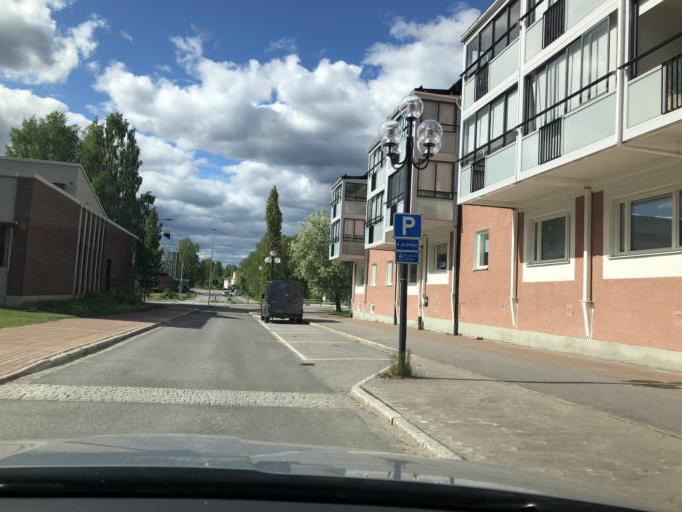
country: SE
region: Norrbotten
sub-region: Alvsbyns Kommun
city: AElvsbyn
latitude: 65.6743
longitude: 21.0072
